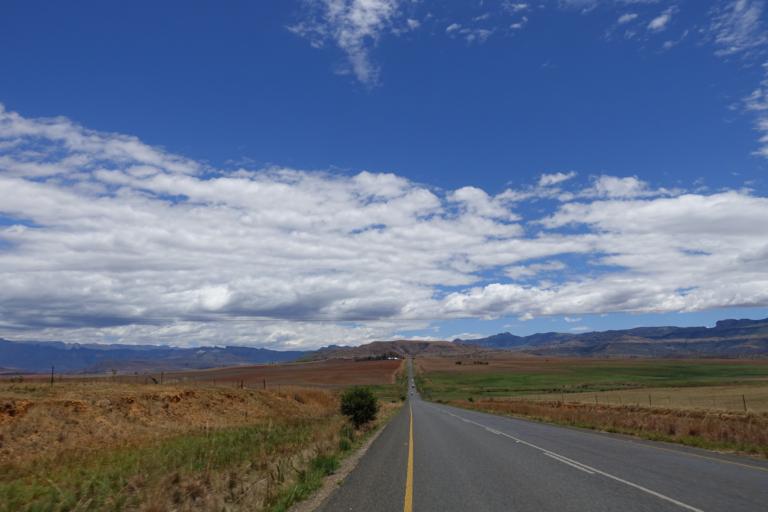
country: ZA
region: KwaZulu-Natal
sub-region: uThukela District Municipality
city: Bergville
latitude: -28.6328
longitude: 29.1372
